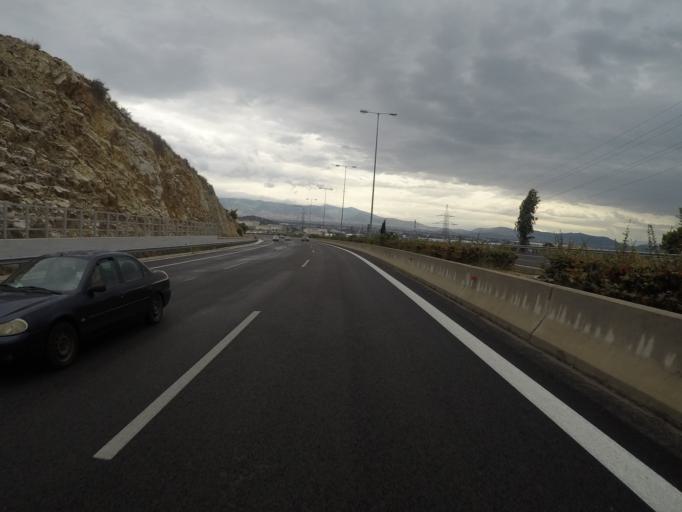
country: GR
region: Attica
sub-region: Nomarchia Dytikis Attikis
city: Mandra
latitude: 38.0297
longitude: 23.4866
